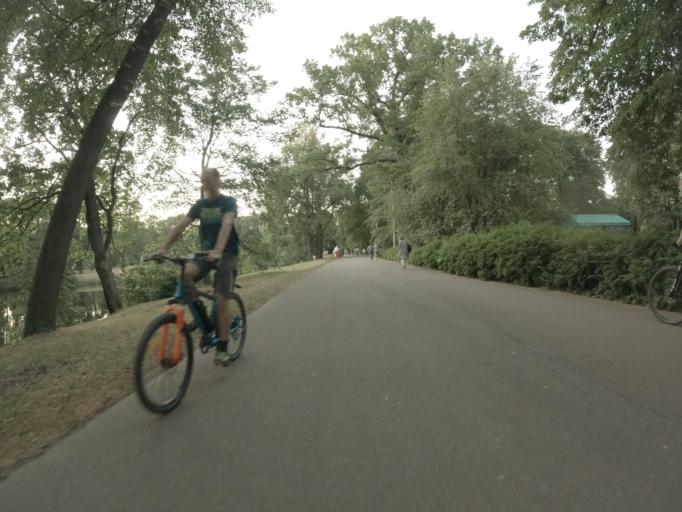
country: RU
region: Leningrad
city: Krestovskiy ostrov
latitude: 59.9777
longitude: 30.2526
